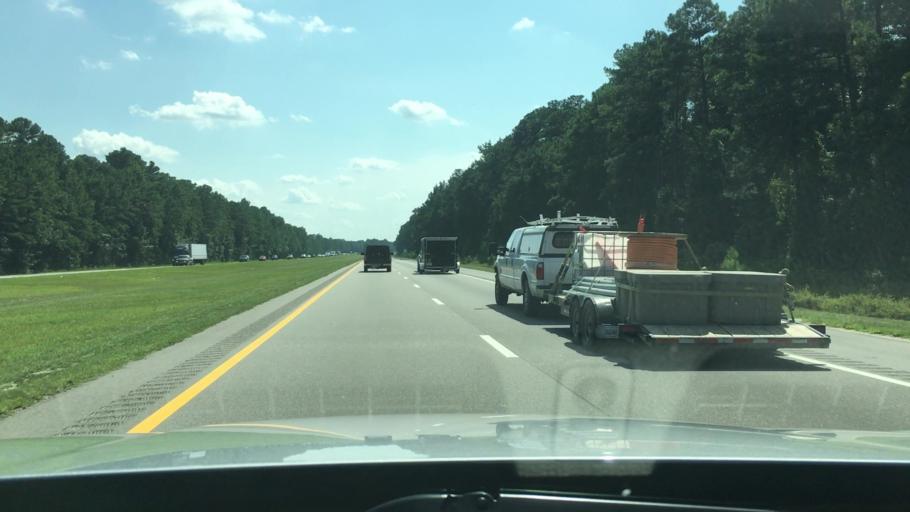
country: US
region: North Carolina
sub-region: Cumberland County
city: Hope Mills
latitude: 34.9555
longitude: -78.8972
